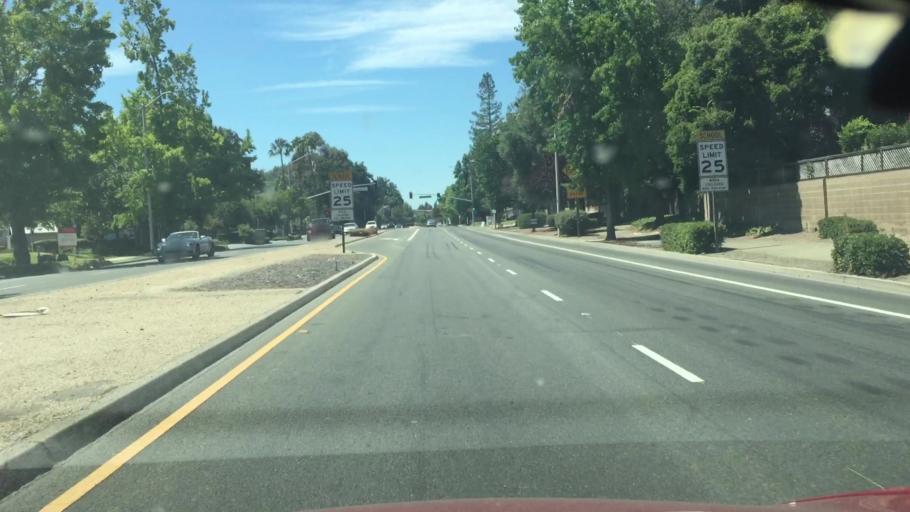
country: US
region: California
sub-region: Alameda County
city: Fremont
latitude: 37.5570
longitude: -121.9511
